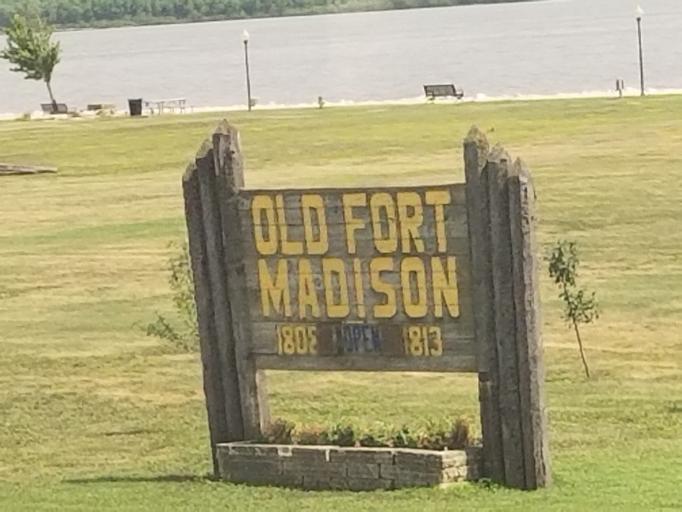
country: US
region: Iowa
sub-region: Lee County
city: Fort Madison
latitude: 40.6295
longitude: -91.3121
